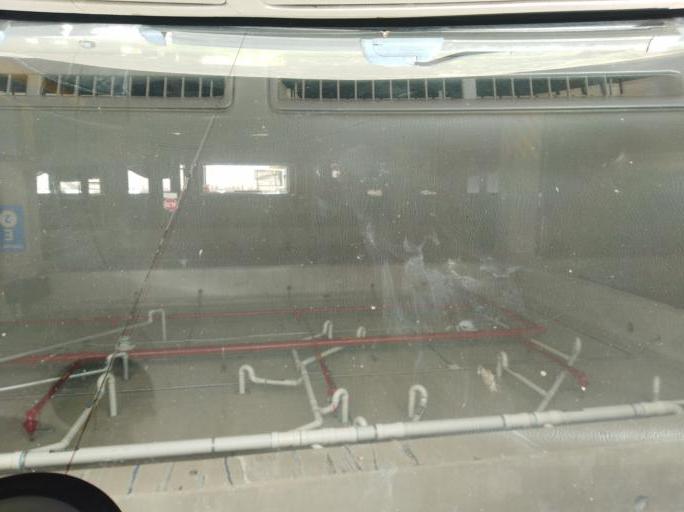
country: NI
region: Managua
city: Managua
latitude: 12.0843
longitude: -86.2303
